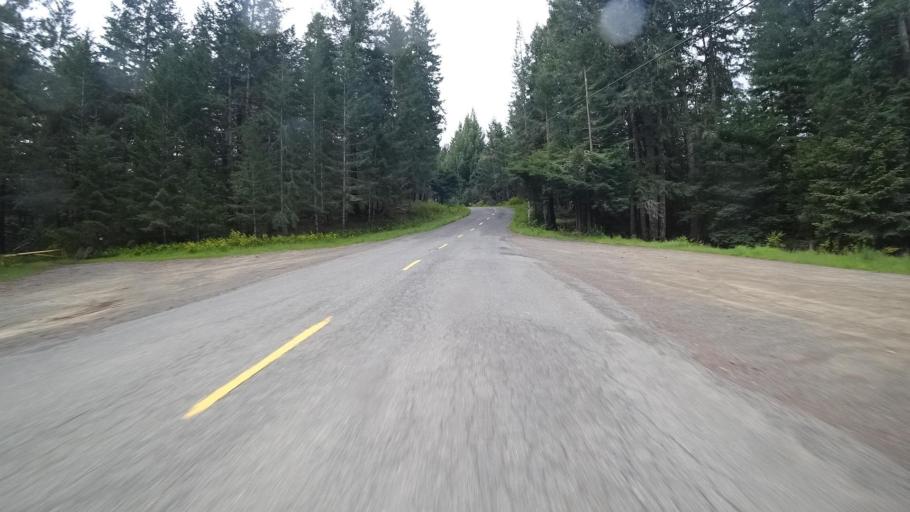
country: US
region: California
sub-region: Humboldt County
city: Redway
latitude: 40.2824
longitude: -123.7978
